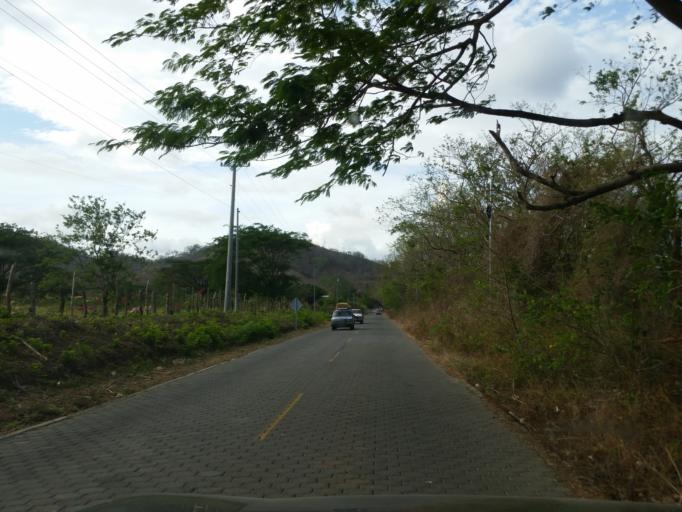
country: NI
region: Rivas
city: Tola
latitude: 11.4047
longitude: -85.9559
